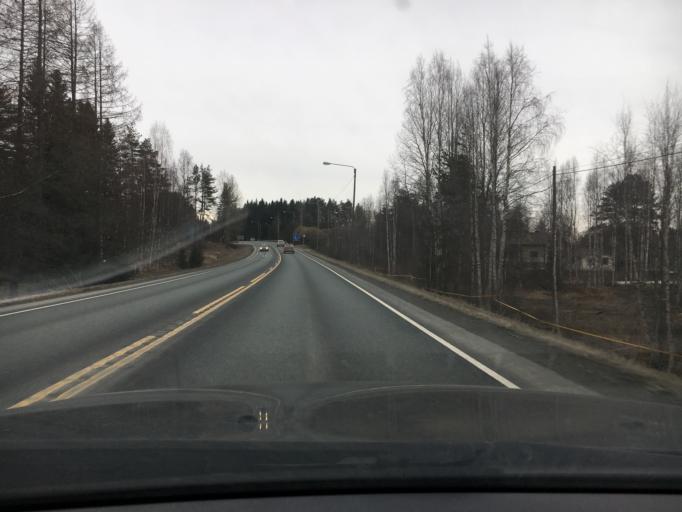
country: FI
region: Northern Savo
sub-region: Kuopio
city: Siilinjaervi
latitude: 63.1121
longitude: 27.6444
